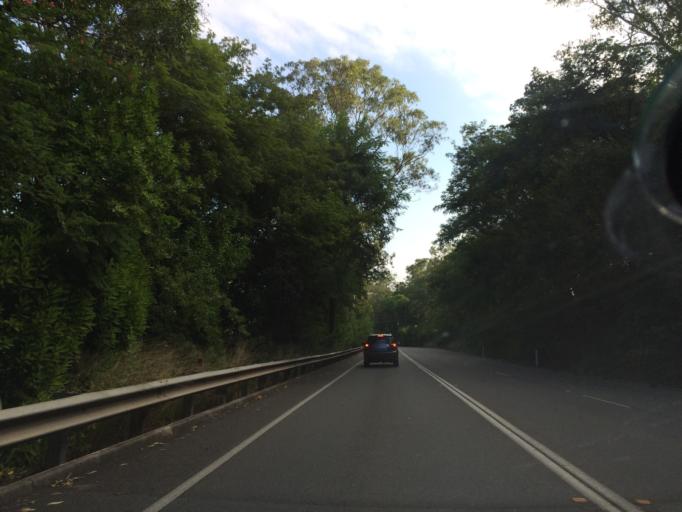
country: AU
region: Queensland
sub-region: Brisbane
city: Kenmore Hills
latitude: -27.5117
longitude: 152.9343
